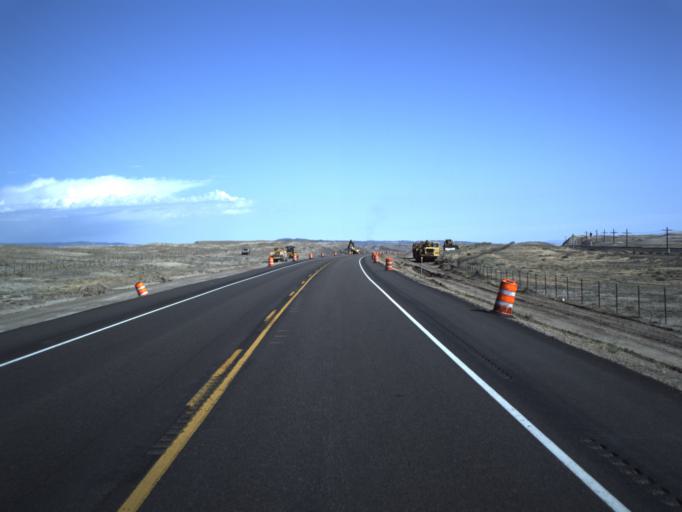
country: US
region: Utah
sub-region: Carbon County
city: East Carbon City
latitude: 39.0289
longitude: -110.3023
